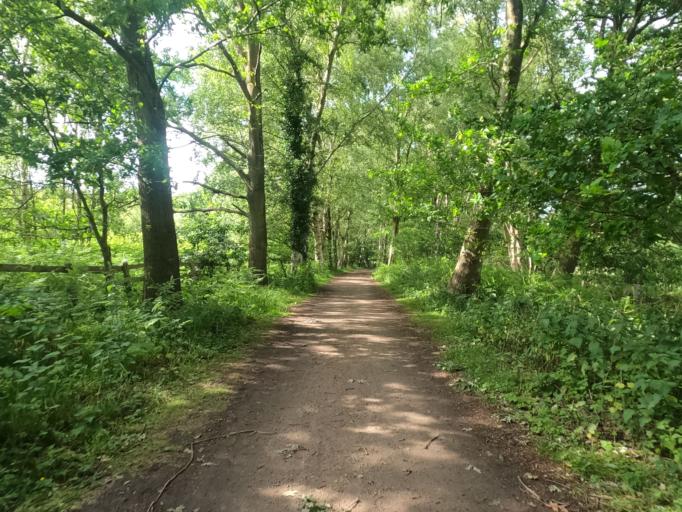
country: GB
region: England
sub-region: Cheshire West and Chester
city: Cuddington
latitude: 53.2250
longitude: -2.6190
